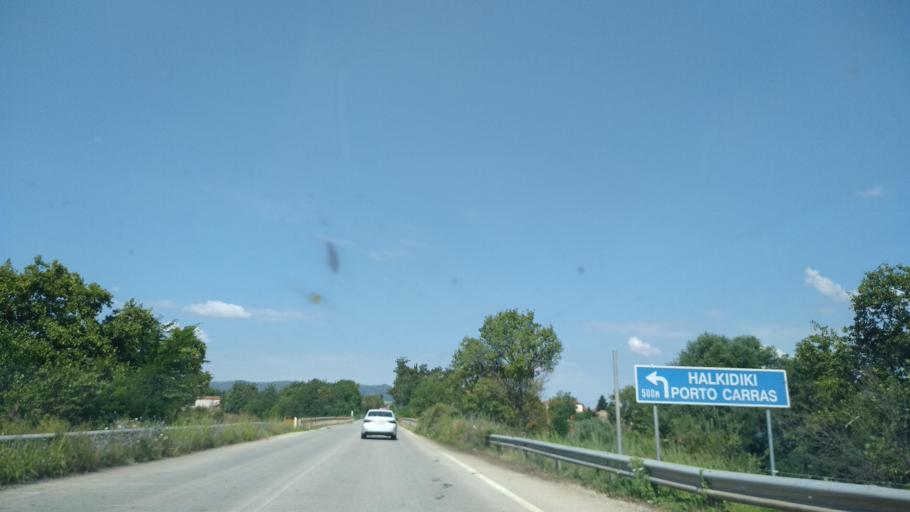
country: GR
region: Central Macedonia
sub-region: Nomos Thessalonikis
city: Nea Apollonia
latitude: 40.6383
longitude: 23.4920
